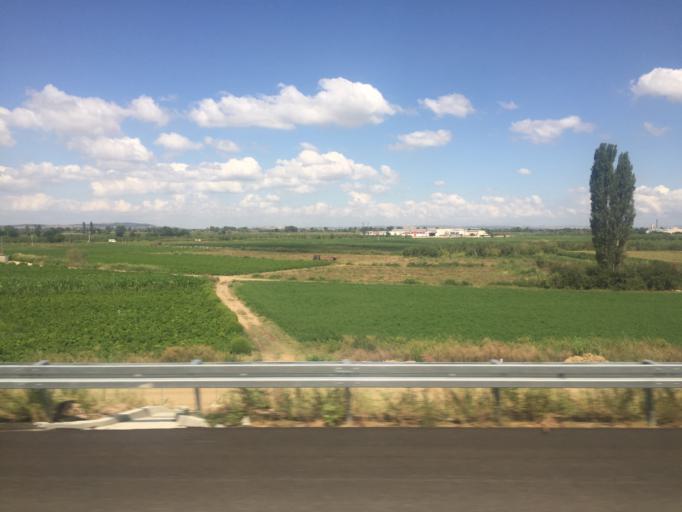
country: TR
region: Balikesir
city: Gobel
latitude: 40.0627
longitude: 28.2432
